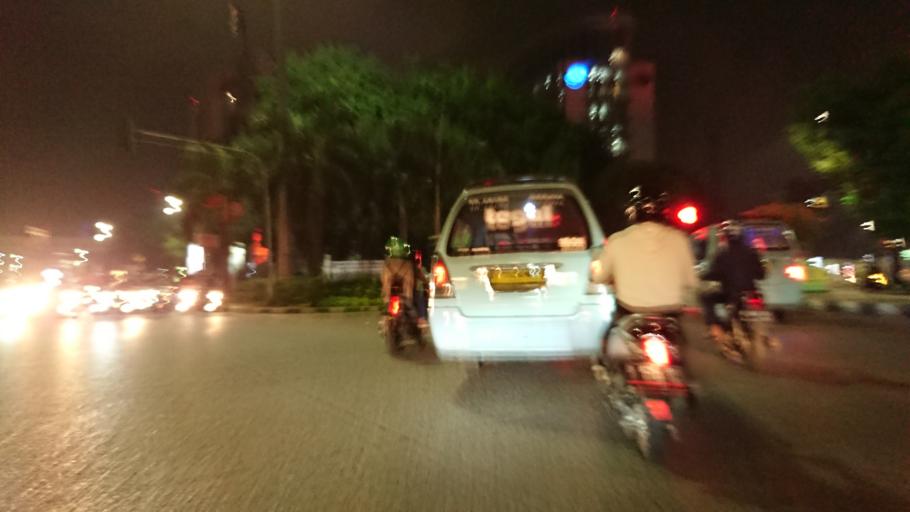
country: ID
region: Jakarta Raya
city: Jakarta
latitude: -6.2011
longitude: 106.7996
